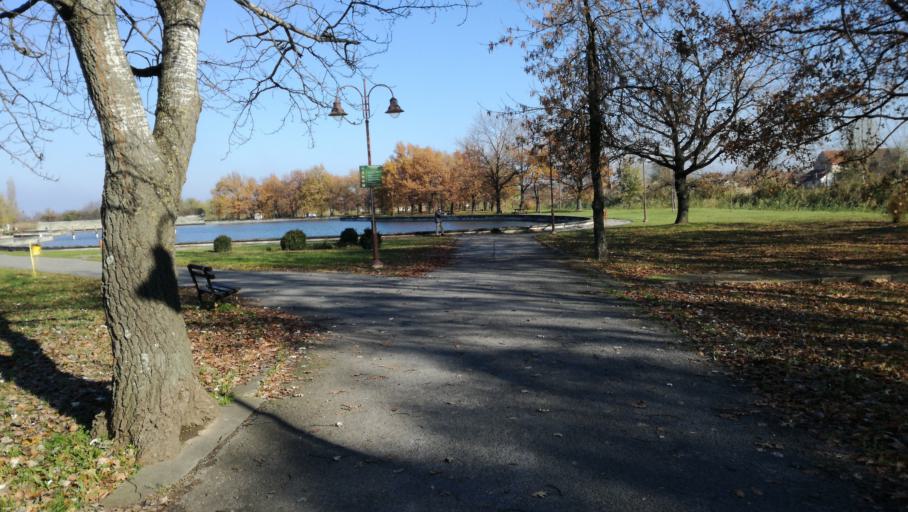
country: RS
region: Autonomna Pokrajina Vojvodina
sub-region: Severnobanatski Okrug
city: Kikinda
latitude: 45.8366
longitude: 20.4660
